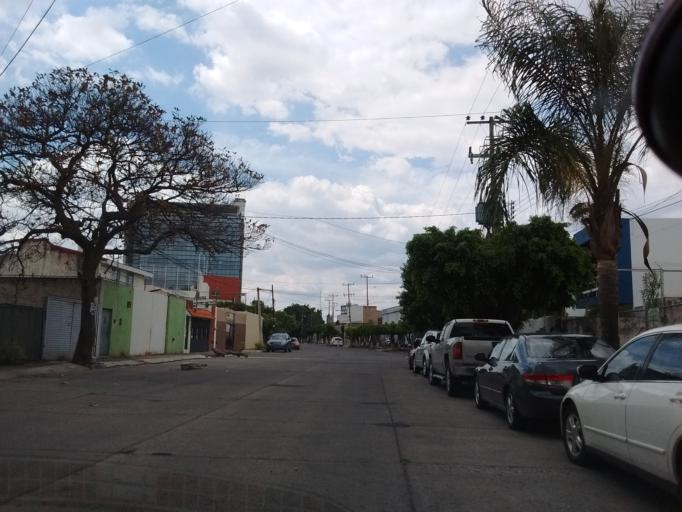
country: MX
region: Jalisco
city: Guadalajara
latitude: 20.6556
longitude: -103.3865
